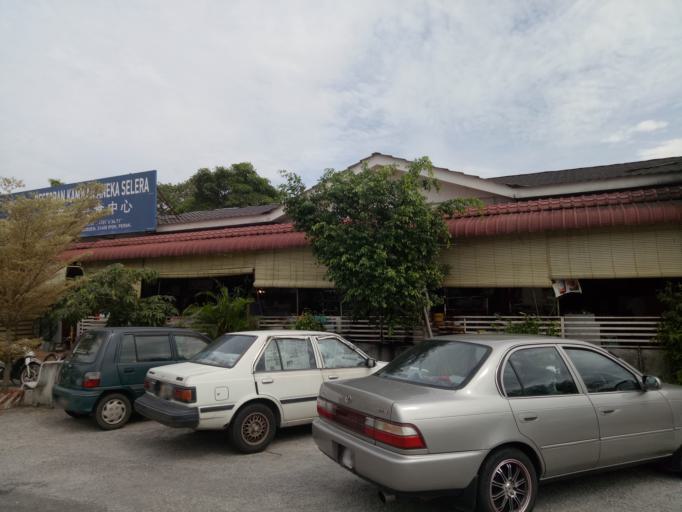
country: MY
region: Perak
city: Ipoh
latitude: 4.6113
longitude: 101.1106
